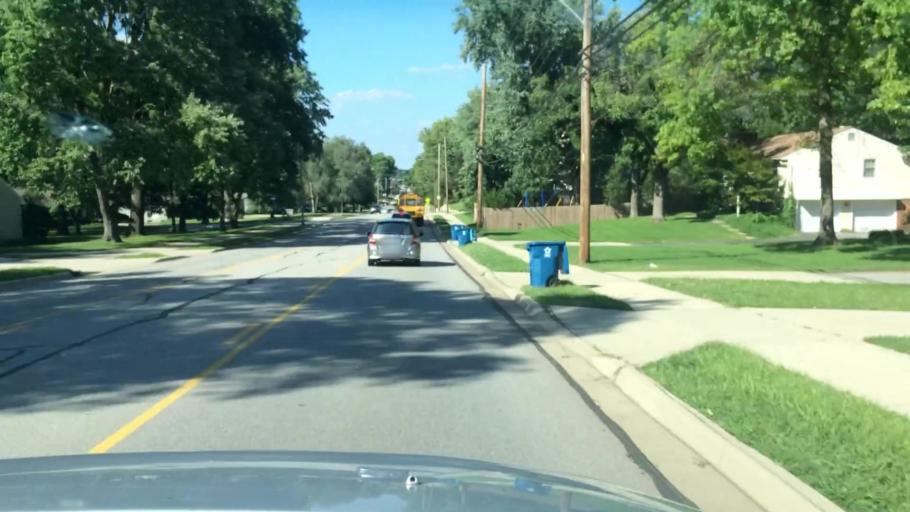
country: US
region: Kansas
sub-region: Johnson County
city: Mission
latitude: 39.0088
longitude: -94.6490
